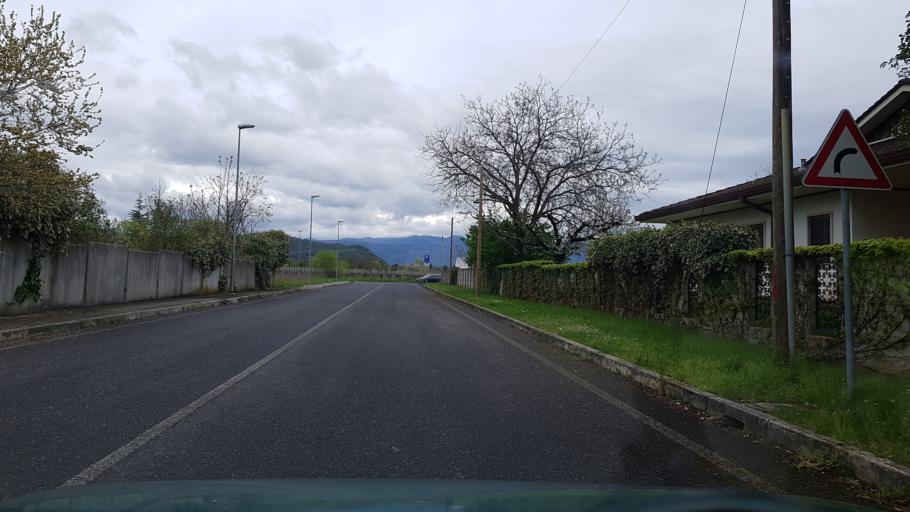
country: IT
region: Friuli Venezia Giulia
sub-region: Provincia di Gorizia
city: Mossa
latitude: 45.9311
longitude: 13.5515
